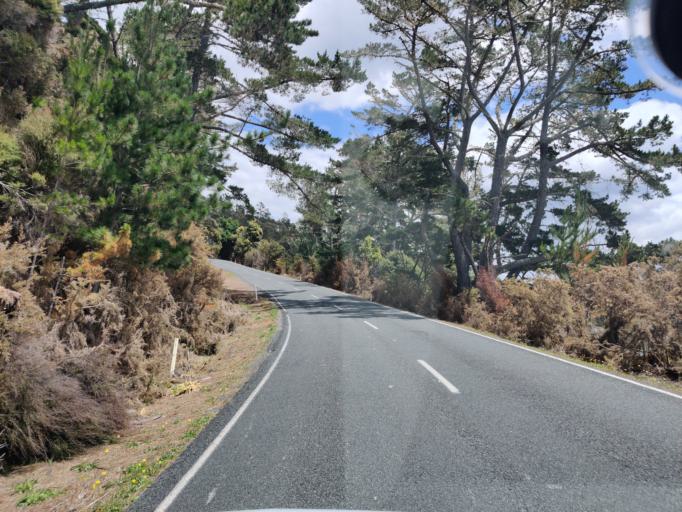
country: NZ
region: Northland
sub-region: Far North District
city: Paihia
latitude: -35.2906
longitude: 174.1414
